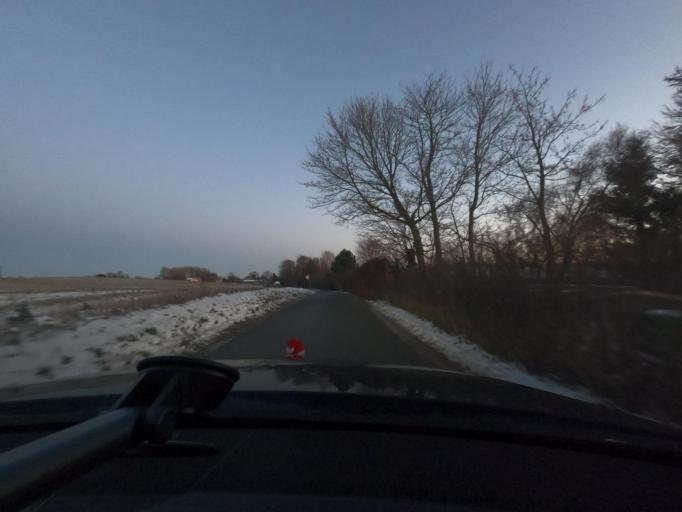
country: DK
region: South Denmark
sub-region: Sonderborg Kommune
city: Horuphav
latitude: 54.8607
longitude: 9.9243
